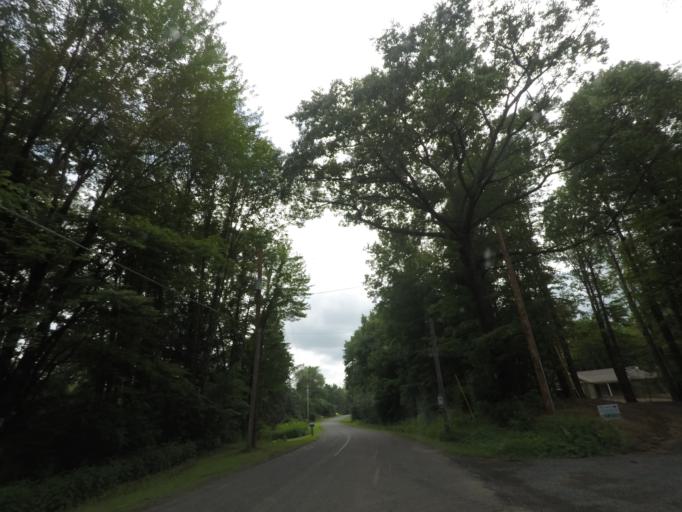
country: US
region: New York
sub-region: Saratoga County
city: Stillwater
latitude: 43.0025
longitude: -73.6869
